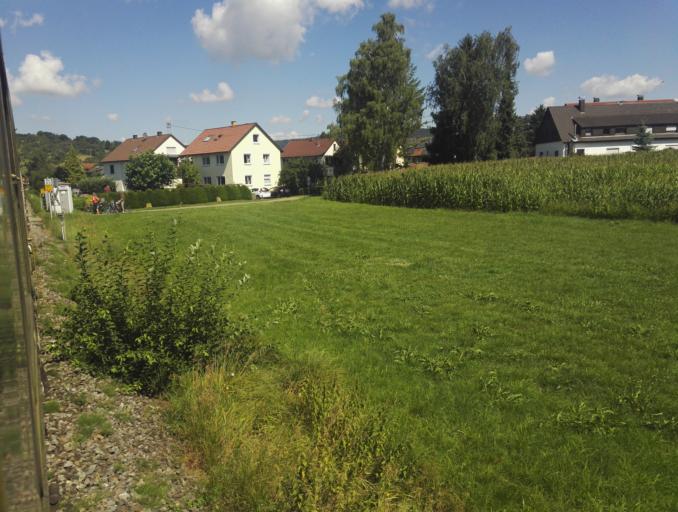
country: DE
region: Baden-Wuerttemberg
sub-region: Regierungsbezirk Stuttgart
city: Rudersberg
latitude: 48.8683
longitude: 9.5294
